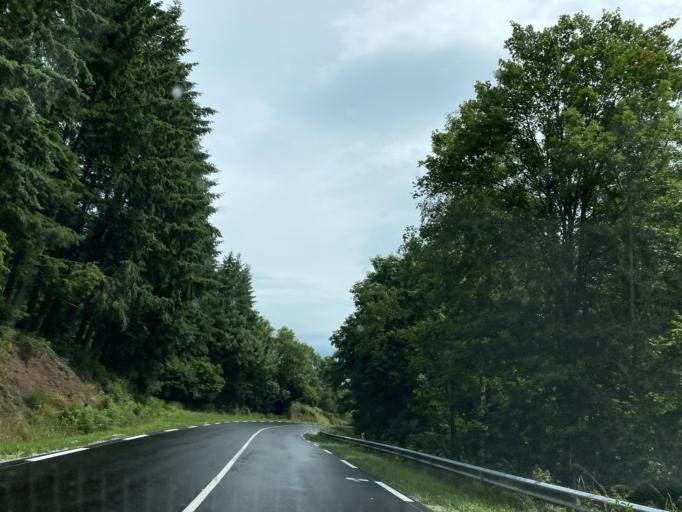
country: FR
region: Rhone-Alpes
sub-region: Departement de la Loire
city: Noiretable
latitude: 45.8140
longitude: 3.8116
